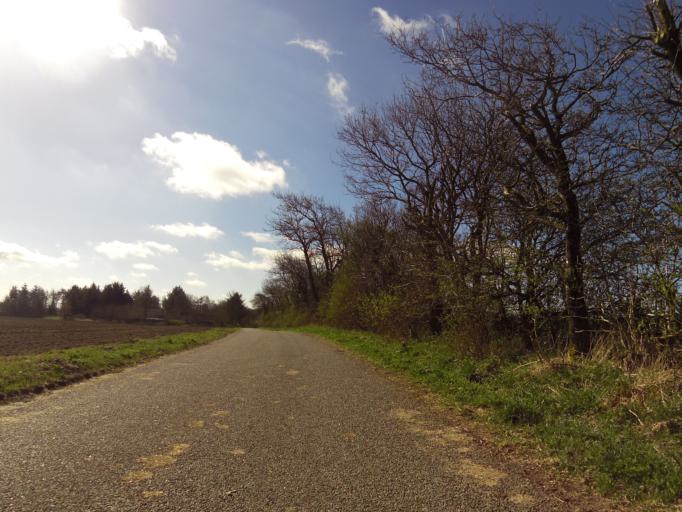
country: DK
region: Central Jutland
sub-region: Holstebro Kommune
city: Vinderup
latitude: 56.4389
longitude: 8.7246
